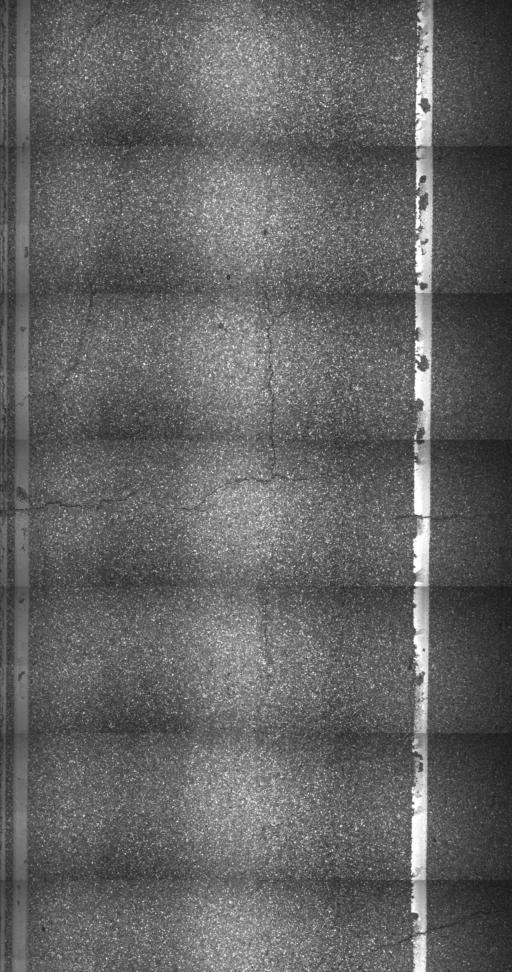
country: US
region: Vermont
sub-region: Lamoille County
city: Morristown
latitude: 44.5032
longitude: -72.6288
